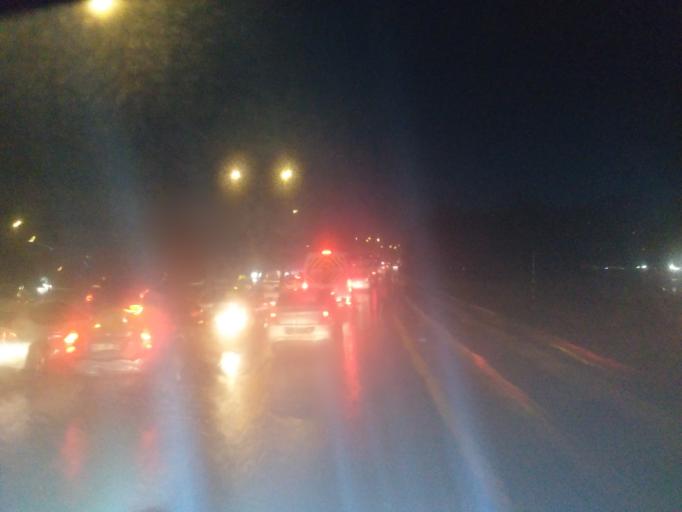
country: TR
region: Ankara
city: Ankara
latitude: 39.9528
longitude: 32.8220
